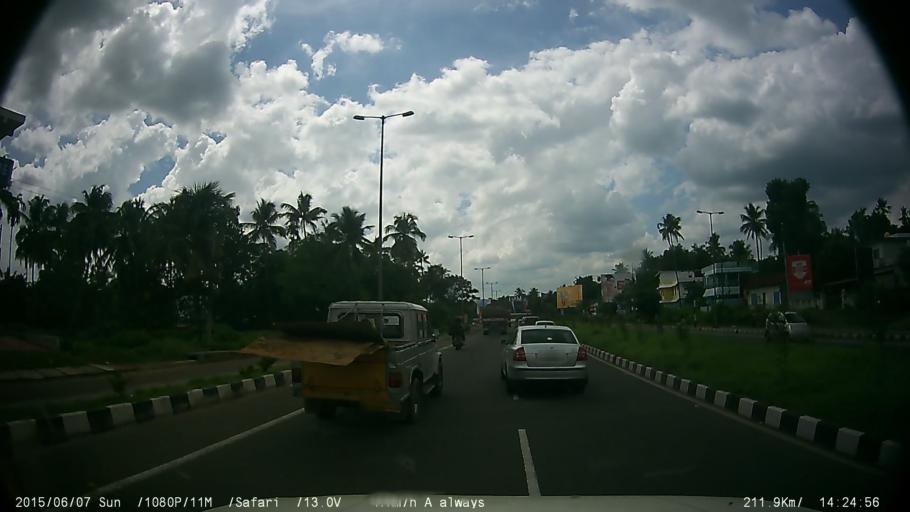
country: IN
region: Kerala
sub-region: Thrissur District
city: Kizhake Chalakudi
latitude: 10.2545
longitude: 76.3666
